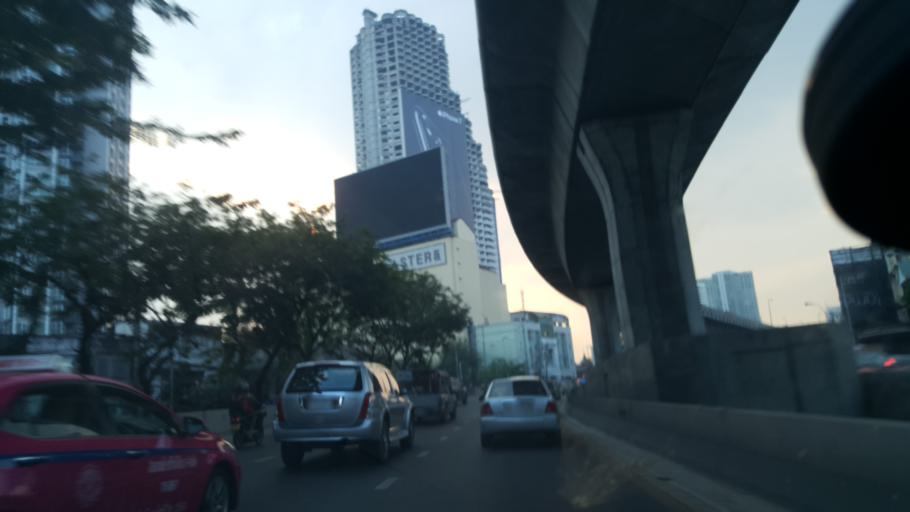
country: TH
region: Bangkok
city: Sathon
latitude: 13.7181
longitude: 100.5176
